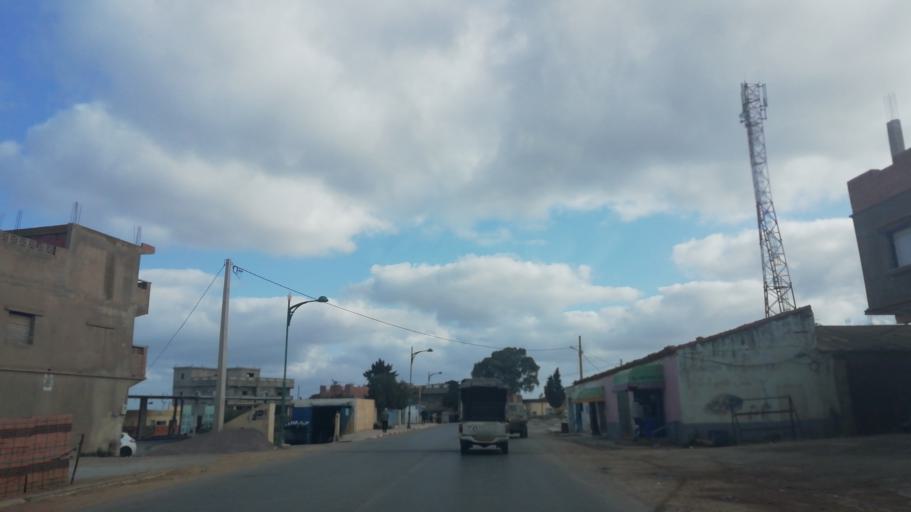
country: DZ
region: Relizane
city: Mazouna
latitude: 36.2621
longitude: 0.6143
